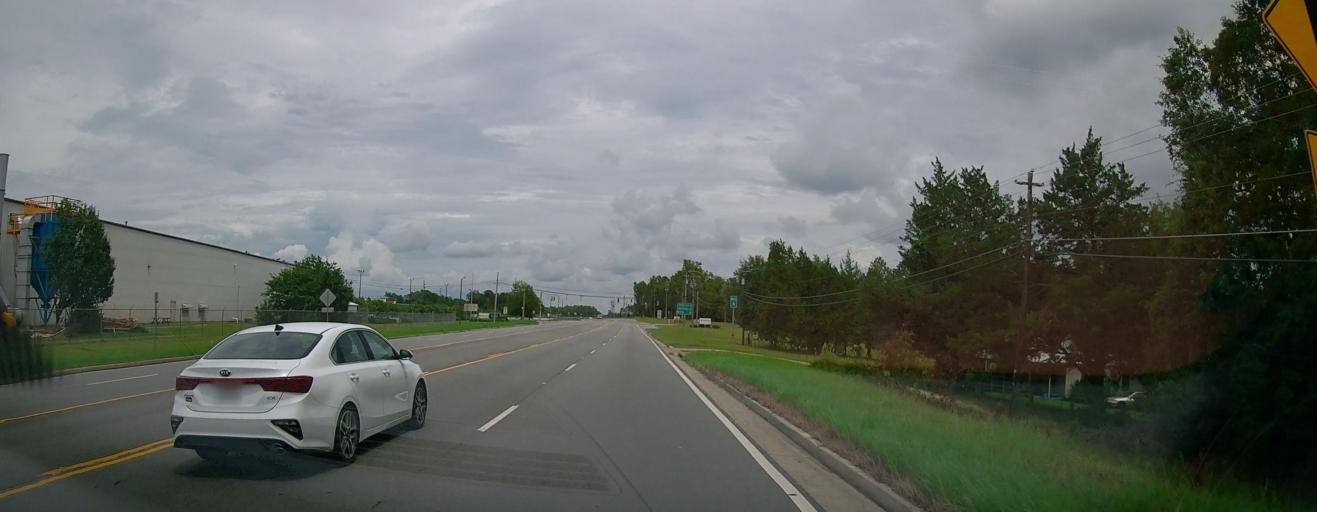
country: US
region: Georgia
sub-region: Telfair County
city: McRae
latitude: 32.0596
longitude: -82.8803
